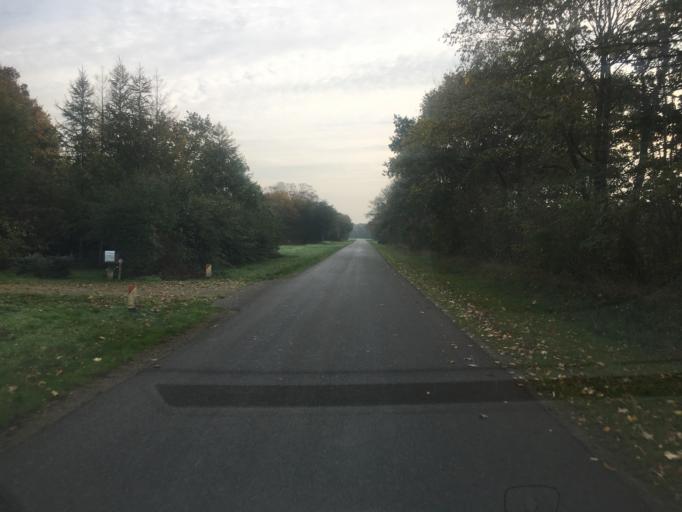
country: DK
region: South Denmark
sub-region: Tonder Kommune
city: Toftlund
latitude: 55.1028
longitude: 9.0643
